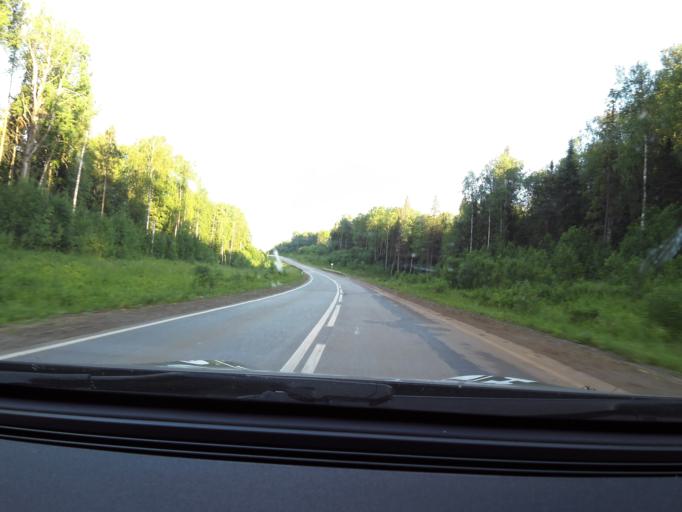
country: RU
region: Kirov
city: Kostino
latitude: 58.6820
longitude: 53.7390
